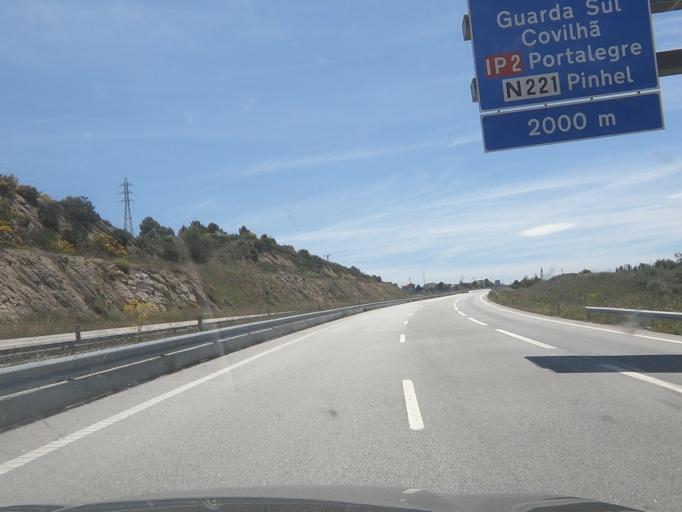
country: PT
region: Guarda
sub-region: Guarda
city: Sequeira
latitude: 40.5665
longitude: -7.2419
